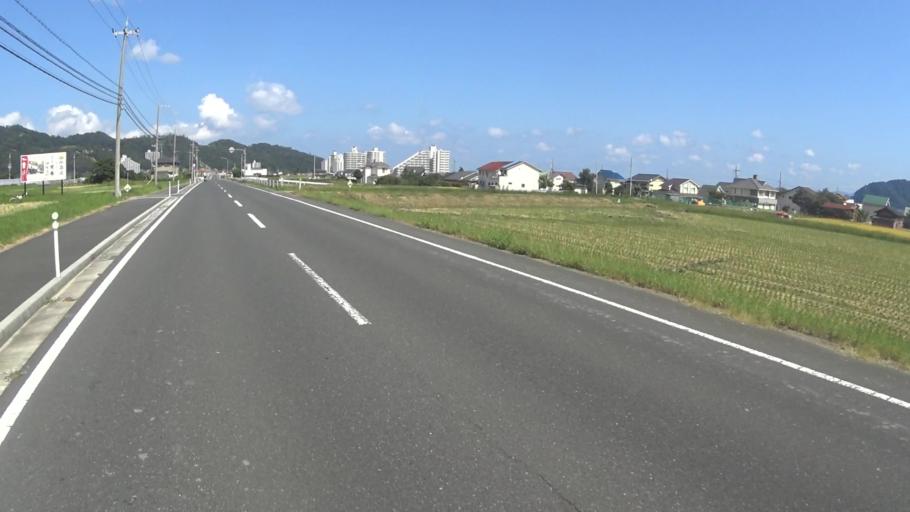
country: JP
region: Kyoto
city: Miyazu
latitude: 35.6060
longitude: 135.2232
